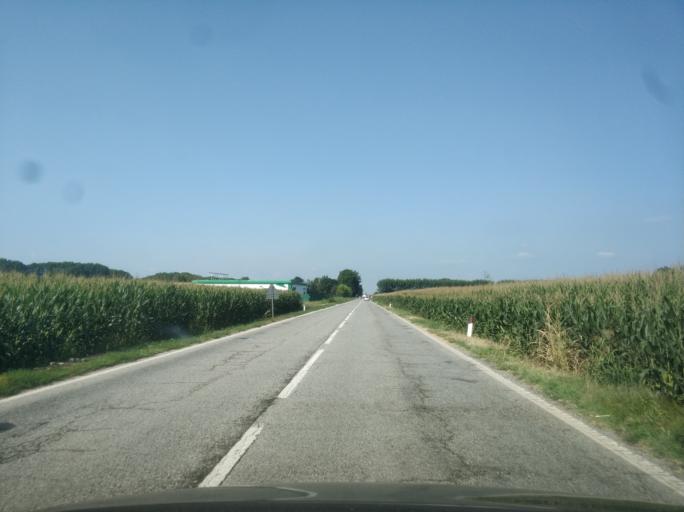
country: IT
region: Piedmont
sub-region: Provincia di Cuneo
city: Centallo
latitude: 44.5239
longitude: 7.6031
